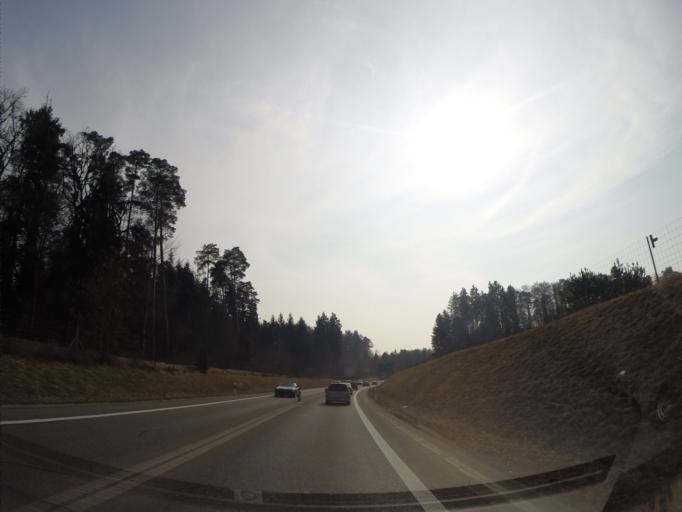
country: CH
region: Zurich
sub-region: Bezirk Andelfingen
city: Henggart
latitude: 47.5586
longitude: 8.6912
